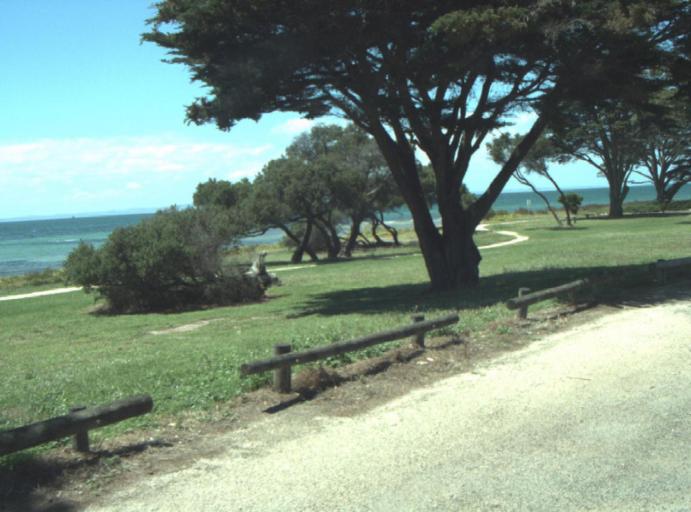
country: AU
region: Victoria
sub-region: Queenscliffe
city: Queenscliff
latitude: -38.1723
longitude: 144.7189
